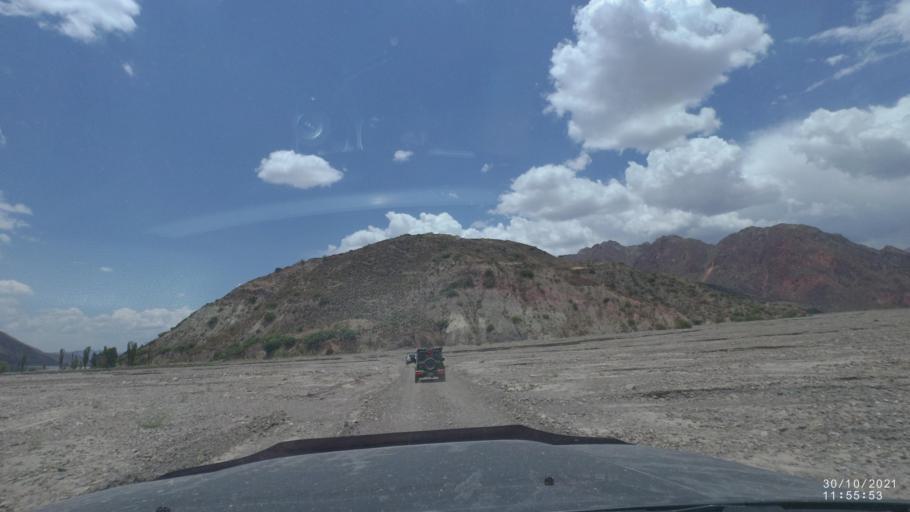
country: BO
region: Cochabamba
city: Colchani
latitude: -17.5212
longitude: -66.6186
